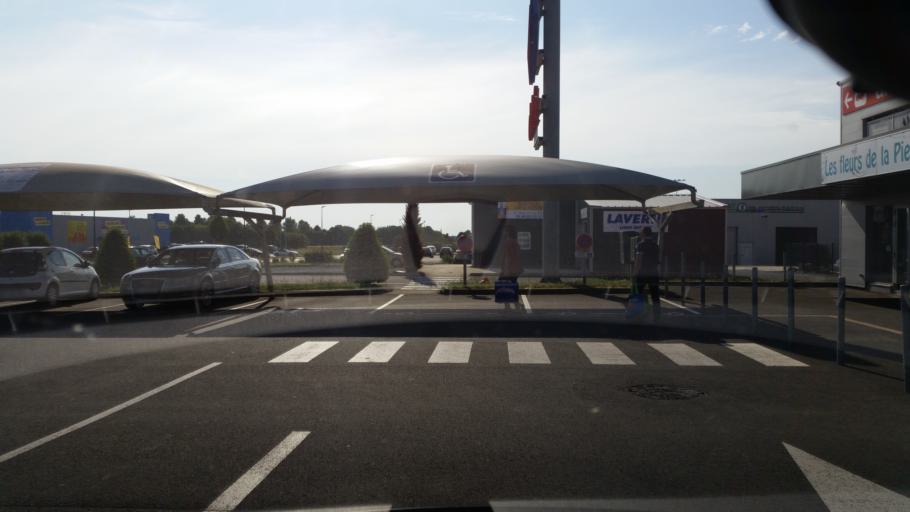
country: FR
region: Poitou-Charentes
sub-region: Departement de la Charente-Maritime
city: Saint-Jean-de-Liversay
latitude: 46.2280
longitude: -0.8735
